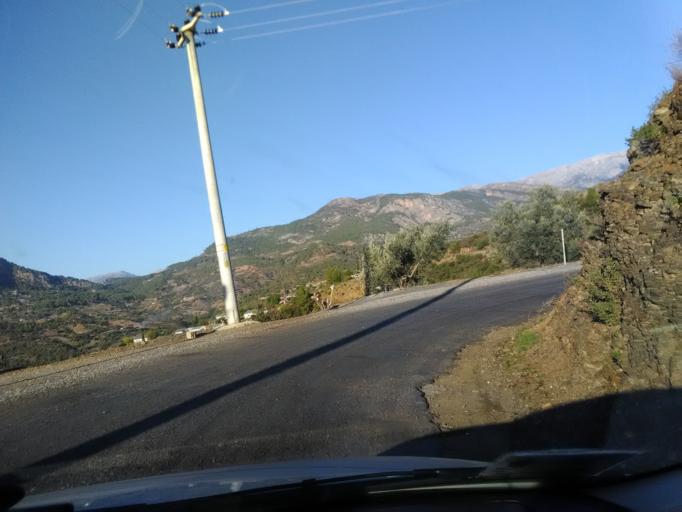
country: TR
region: Antalya
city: Gazipasa
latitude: 36.3090
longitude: 32.4067
